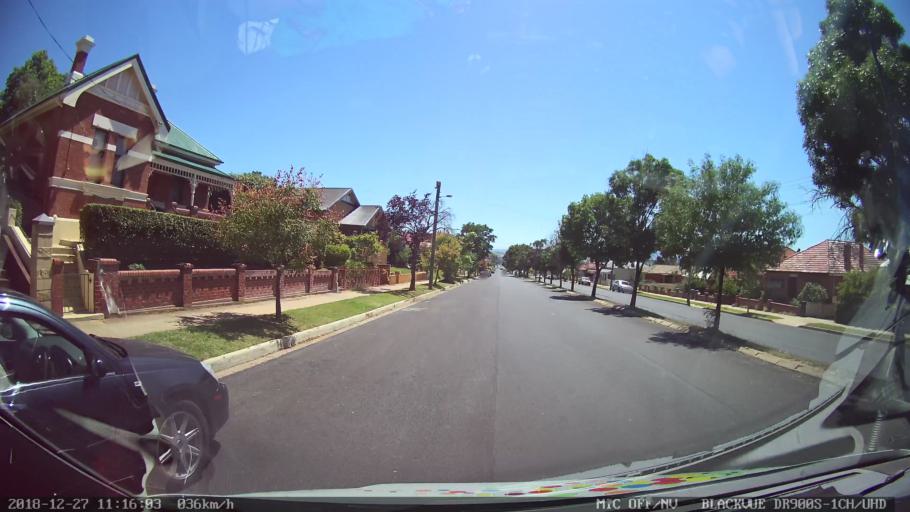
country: AU
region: New South Wales
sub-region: Bathurst Regional
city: Bathurst
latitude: -33.4238
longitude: 149.5725
